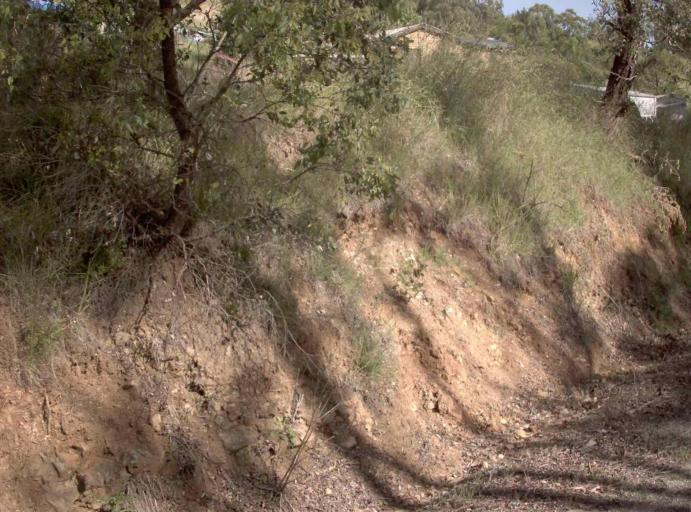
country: AU
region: Victoria
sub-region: East Gippsland
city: Lakes Entrance
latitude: -37.5029
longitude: 148.1705
